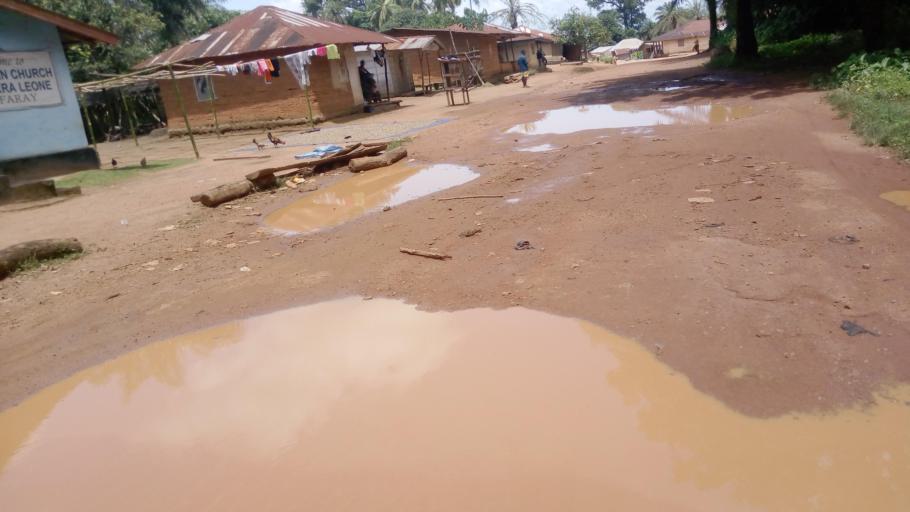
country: SL
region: Northern Province
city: Binkolo
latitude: 8.9552
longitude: -11.9667
